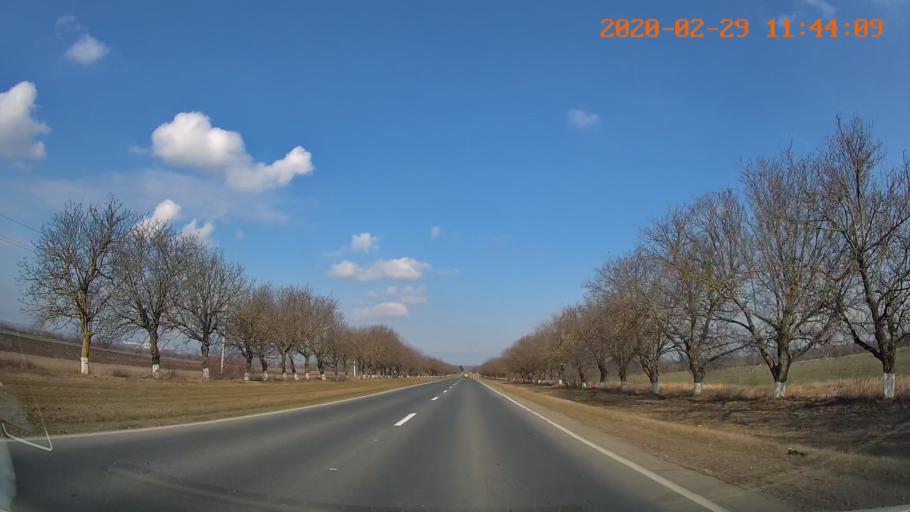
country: MD
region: Rezina
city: Saharna
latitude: 47.7069
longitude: 29.0010
